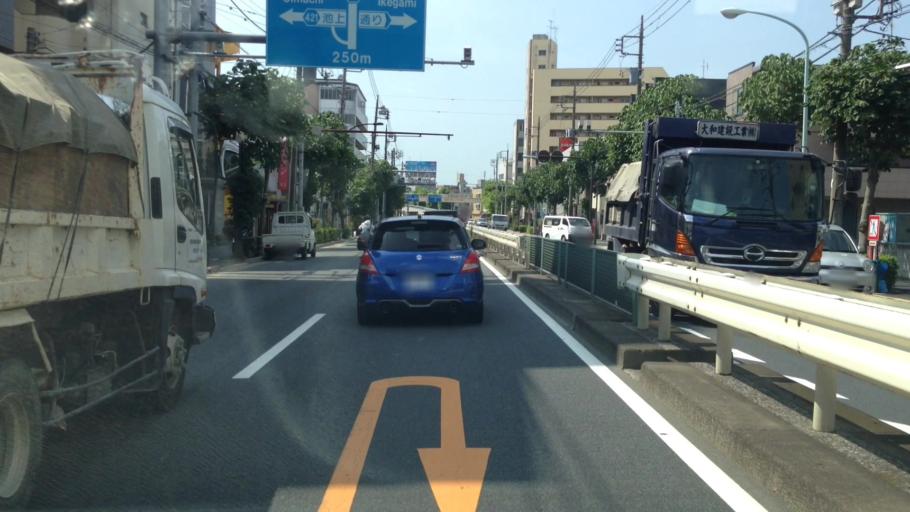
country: JP
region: Kanagawa
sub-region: Kawasaki-shi
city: Kawasaki
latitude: 35.5850
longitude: 139.7200
